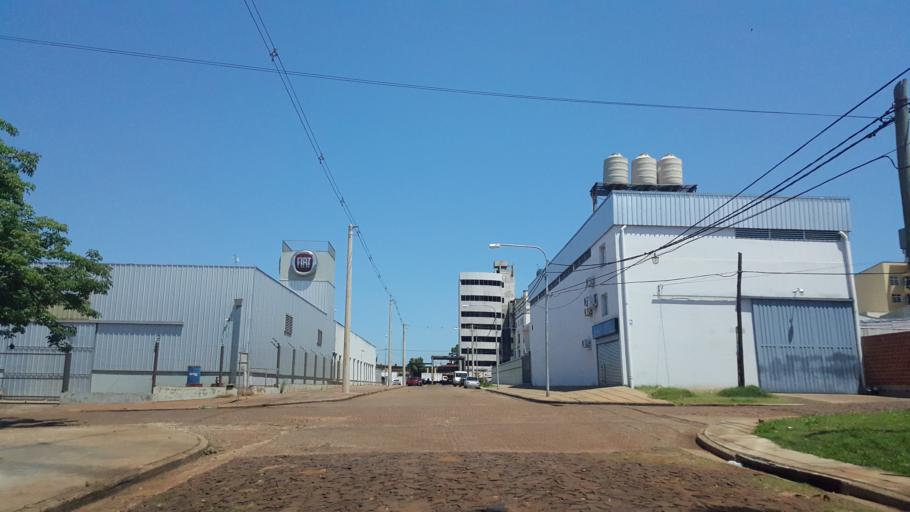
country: AR
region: Misiones
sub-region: Departamento de Capital
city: Posadas
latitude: -27.3922
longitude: -55.9092
